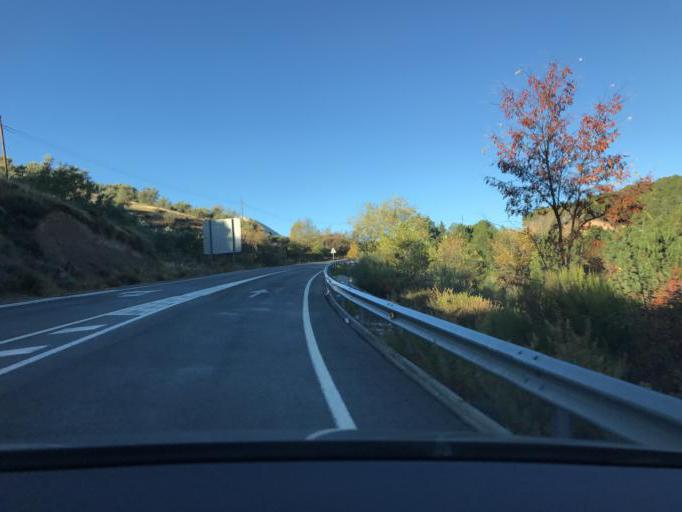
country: ES
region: Andalusia
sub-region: Provincia de Granada
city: Huetor Santillan
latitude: 37.2248
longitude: -3.5337
